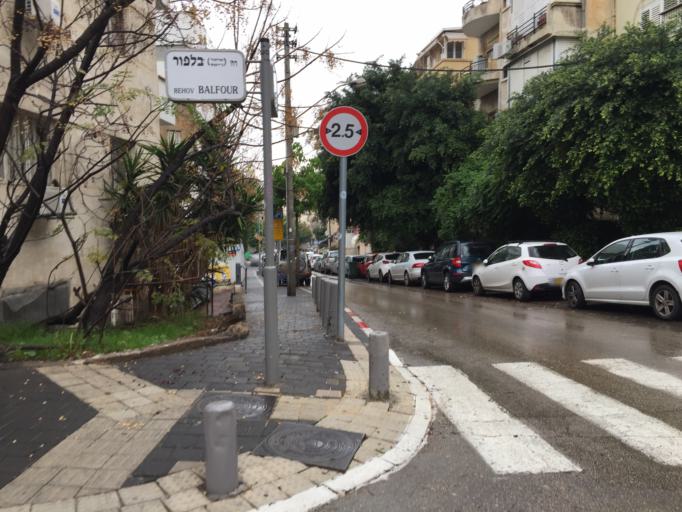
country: IL
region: Tel Aviv
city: Tel Aviv
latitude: 32.0679
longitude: 34.7729
